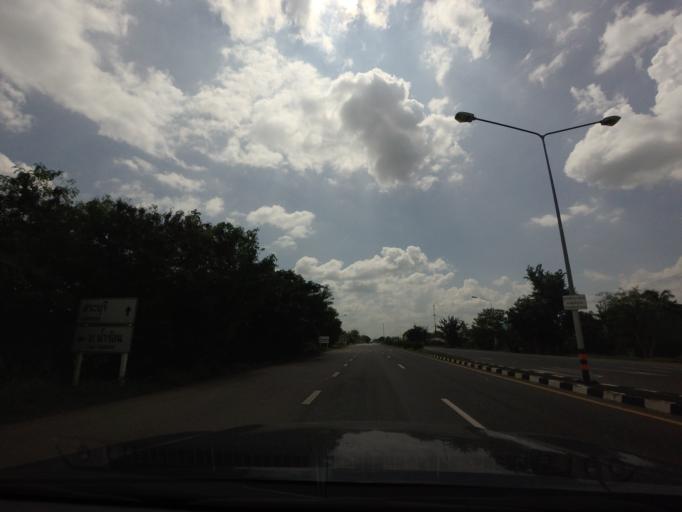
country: TH
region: Phetchabun
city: Nong Phai
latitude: 16.1652
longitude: 101.0731
